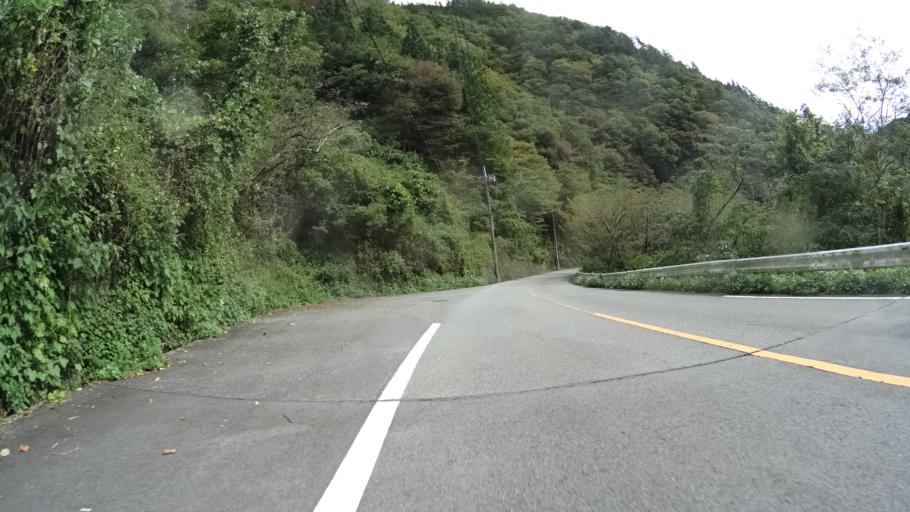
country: JP
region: Yamanashi
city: Otsuki
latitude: 35.7846
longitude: 138.9752
